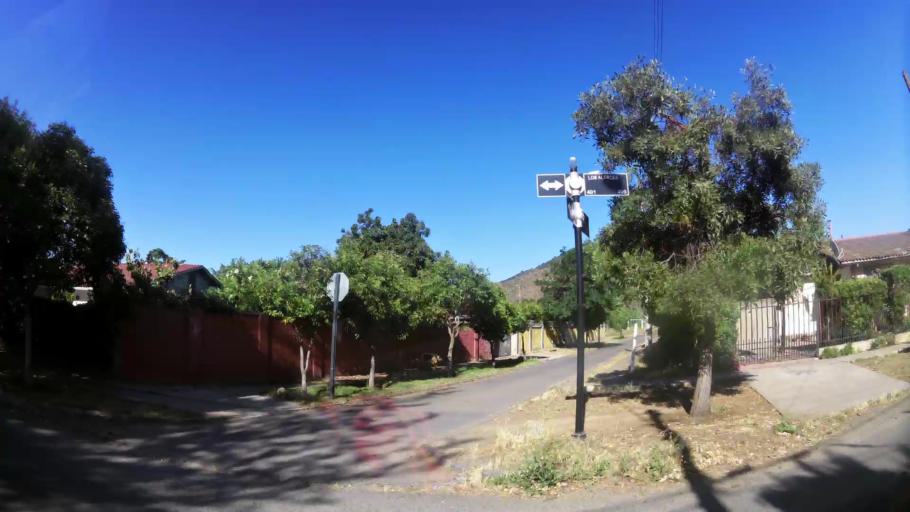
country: CL
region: Santiago Metropolitan
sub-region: Provincia de Chacabuco
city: Lampa
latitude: -33.3972
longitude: -71.1222
